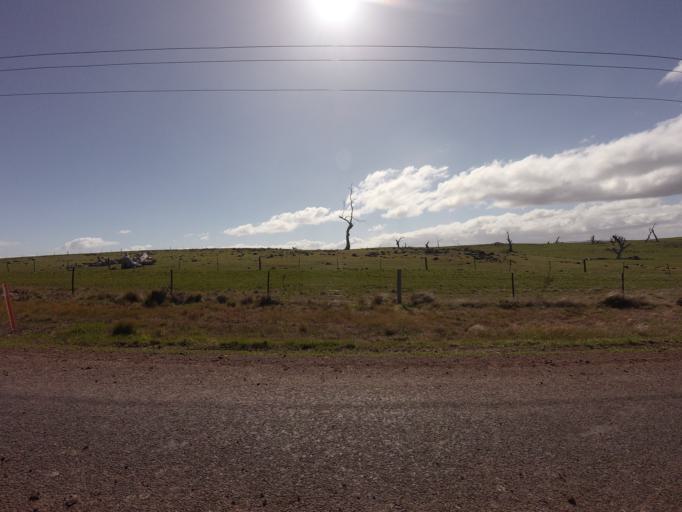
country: AU
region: Tasmania
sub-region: Northern Midlands
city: Evandale
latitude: -41.8958
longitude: 147.4308
